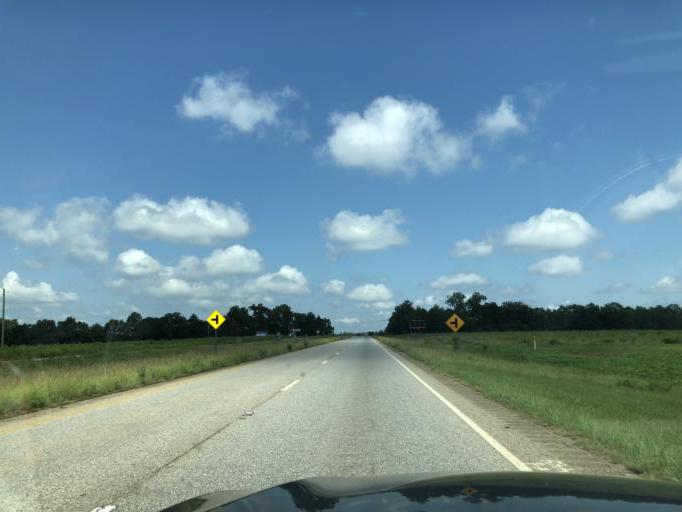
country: US
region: Alabama
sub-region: Henry County
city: Abbeville
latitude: 31.6175
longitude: -85.2775
